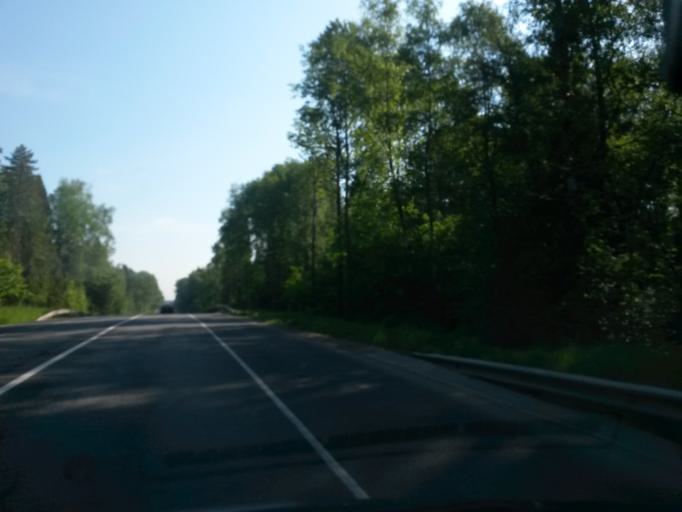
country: RU
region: Jaroslavl
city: Pereslavl'-Zalesskiy
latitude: 56.8567
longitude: 38.9430
